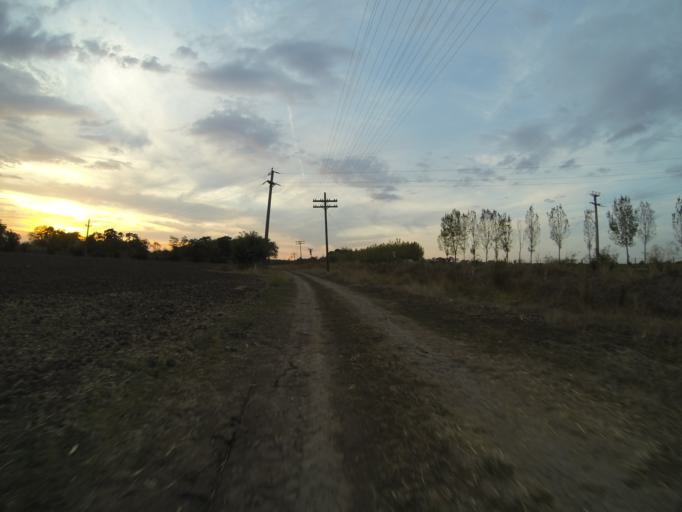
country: RO
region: Dolj
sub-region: Comuna Segarcea
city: Segarcea
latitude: 44.1006
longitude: 23.7220
